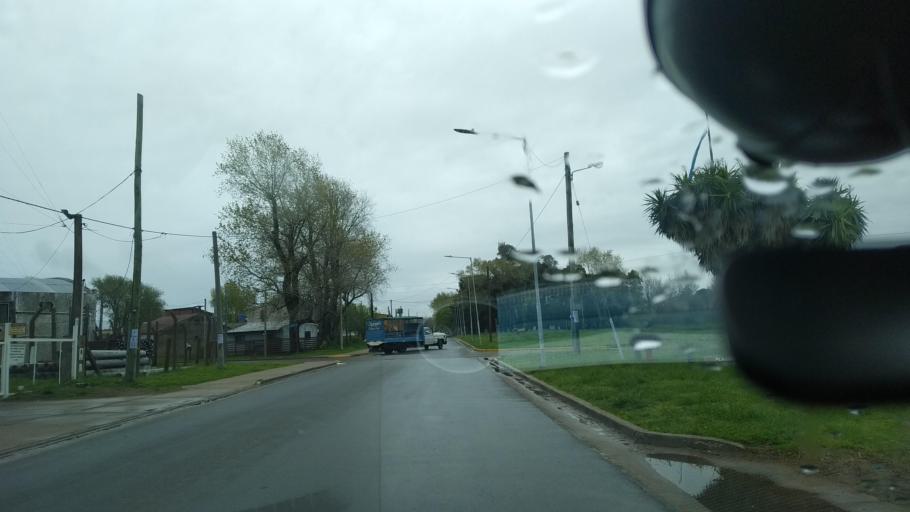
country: AR
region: Buenos Aires
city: Mar del Tuyu
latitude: -36.5369
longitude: -56.7120
